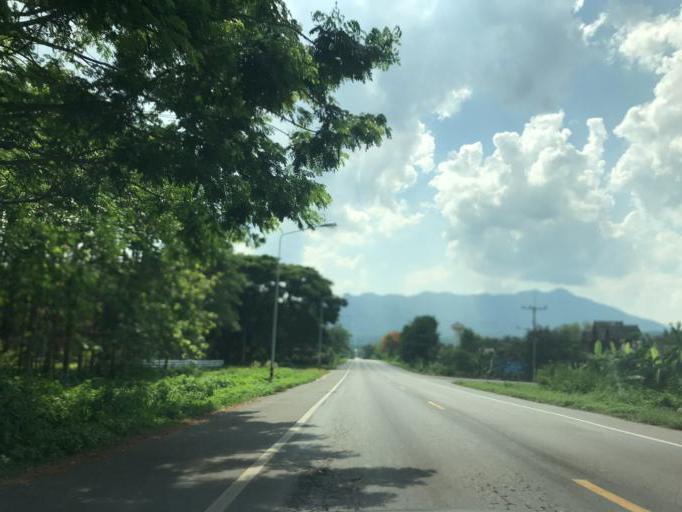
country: TH
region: Phayao
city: Phayao
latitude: 19.0906
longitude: 99.8372
